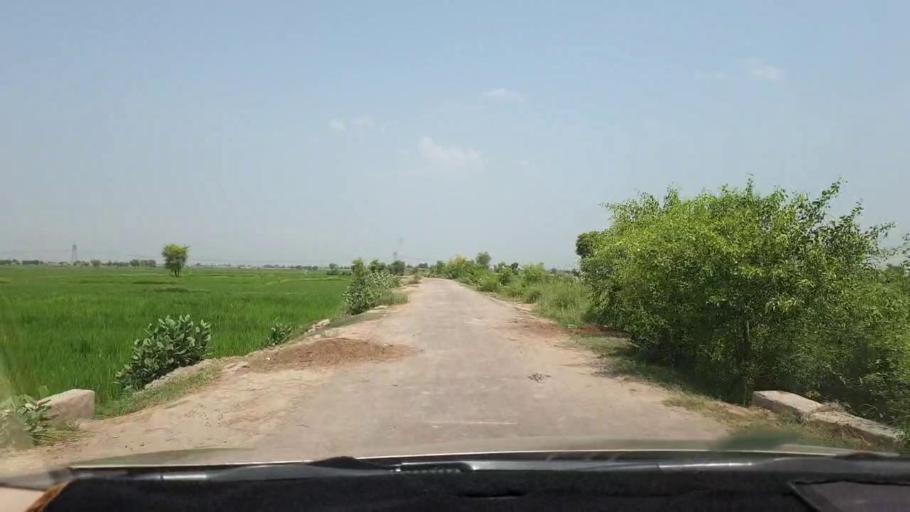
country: PK
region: Sindh
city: Naudero
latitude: 27.6642
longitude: 68.3245
